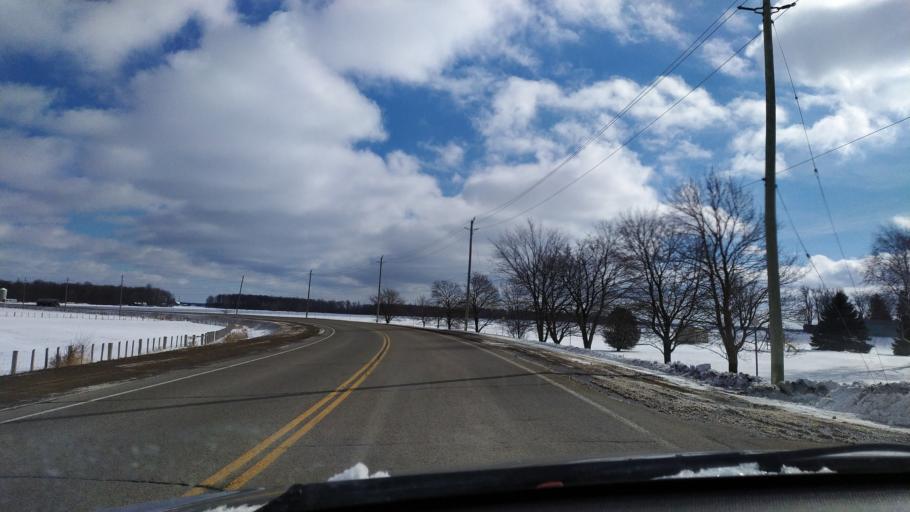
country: CA
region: Ontario
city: Waterloo
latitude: 43.5812
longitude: -80.6088
